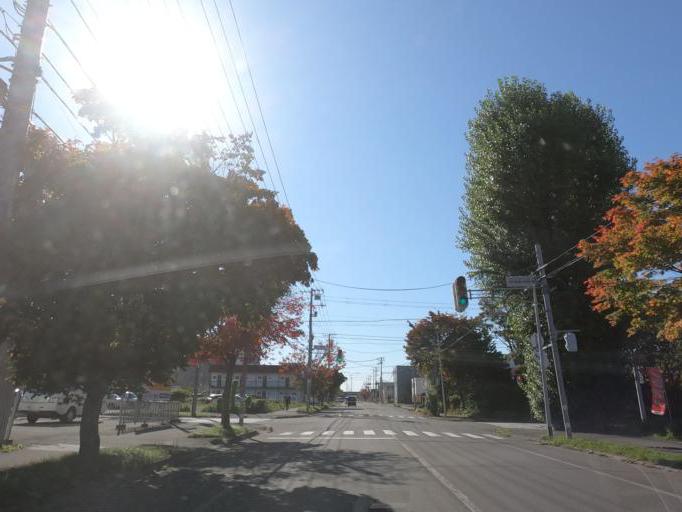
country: JP
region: Hokkaido
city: Obihiro
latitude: 42.9190
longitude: 143.2120
